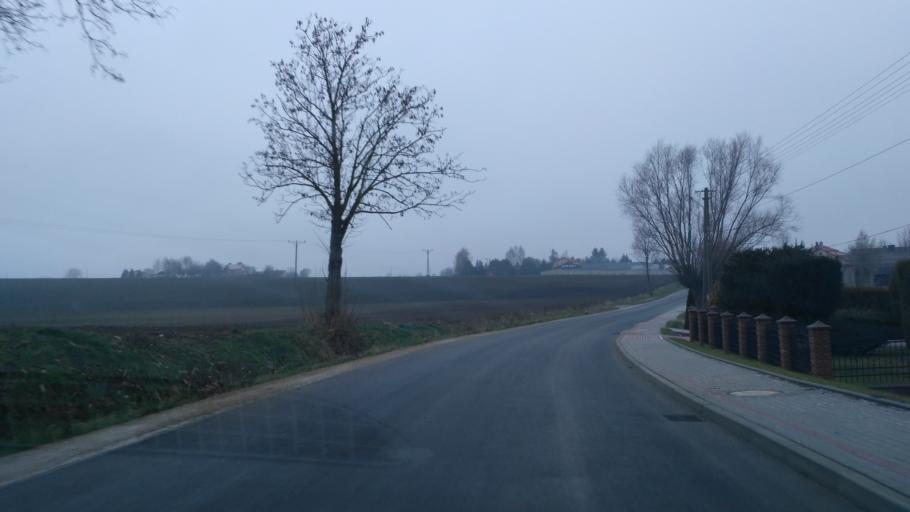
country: PL
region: Subcarpathian Voivodeship
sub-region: Powiat przeworski
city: Kanczuga
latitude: 50.0110
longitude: 22.4255
